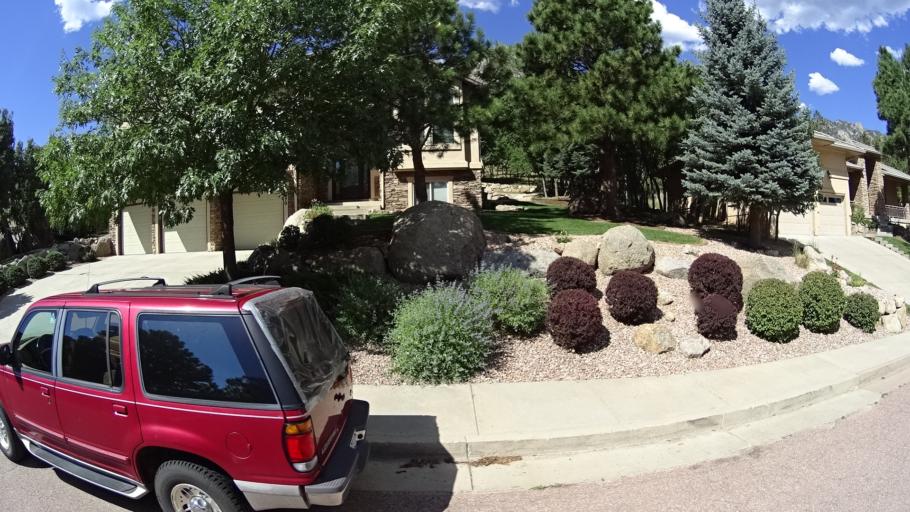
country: US
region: Colorado
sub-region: El Paso County
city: Fort Carson
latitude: 38.7427
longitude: -104.8365
